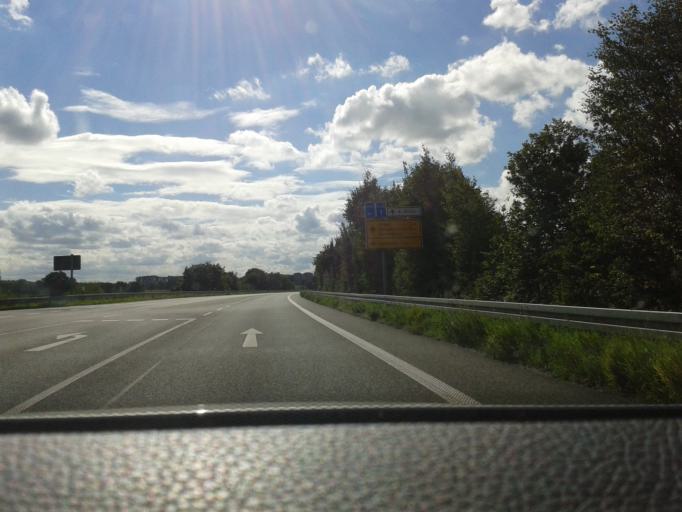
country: DE
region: North Rhine-Westphalia
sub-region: Regierungsbezirk Dusseldorf
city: Uedem
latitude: 51.6313
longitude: 6.2877
